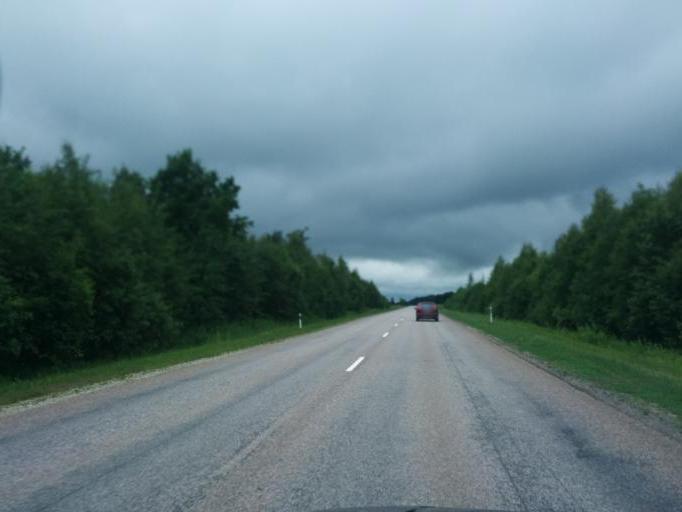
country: LV
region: Beverina
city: Murmuiza
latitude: 57.4822
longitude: 25.6104
